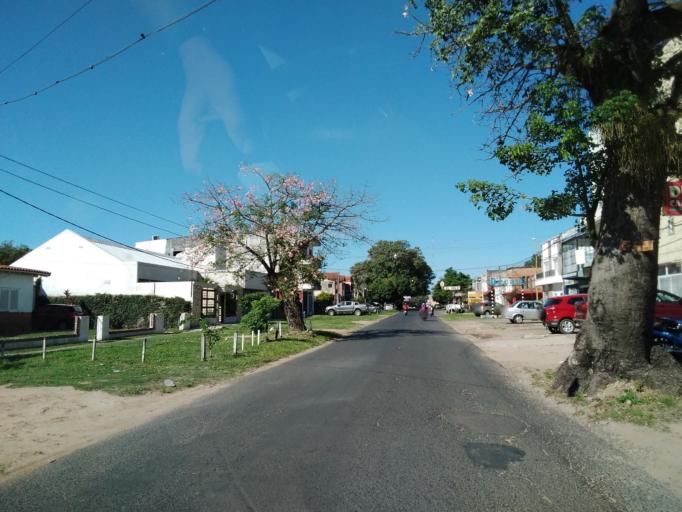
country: AR
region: Corrientes
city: Corrientes
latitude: -27.4707
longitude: -58.8161
